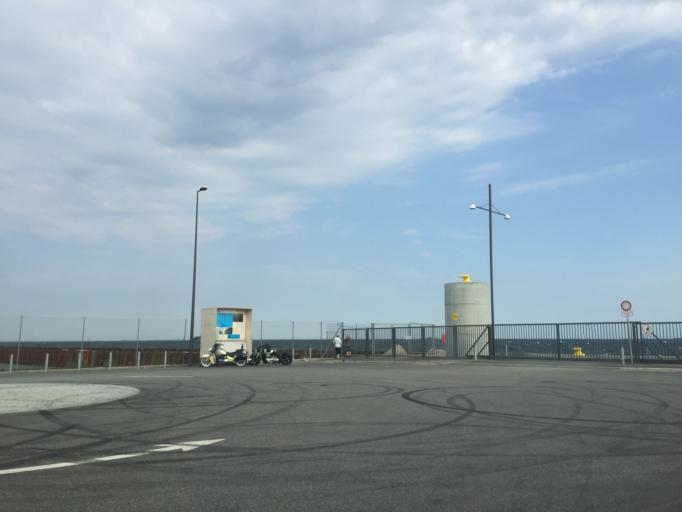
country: DK
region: Capital Region
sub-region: Gentofte Kommune
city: Charlottenlund
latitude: 55.7186
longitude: 12.6303
